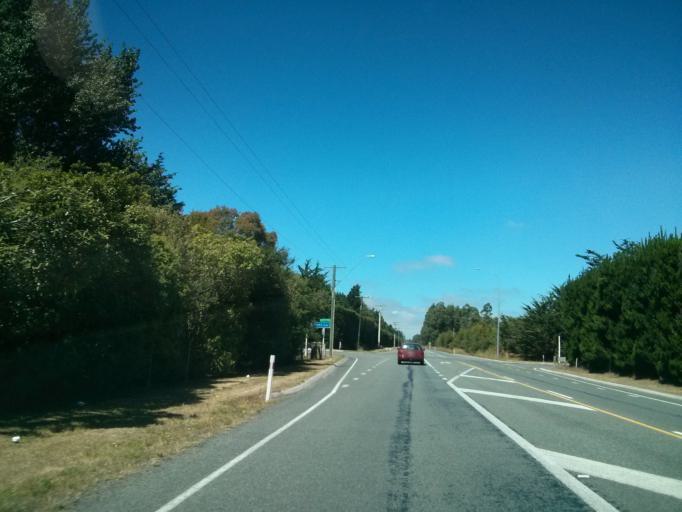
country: NZ
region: Canterbury
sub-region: Waimakariri District
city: Kaiapoi
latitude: -43.3855
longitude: 172.5580
